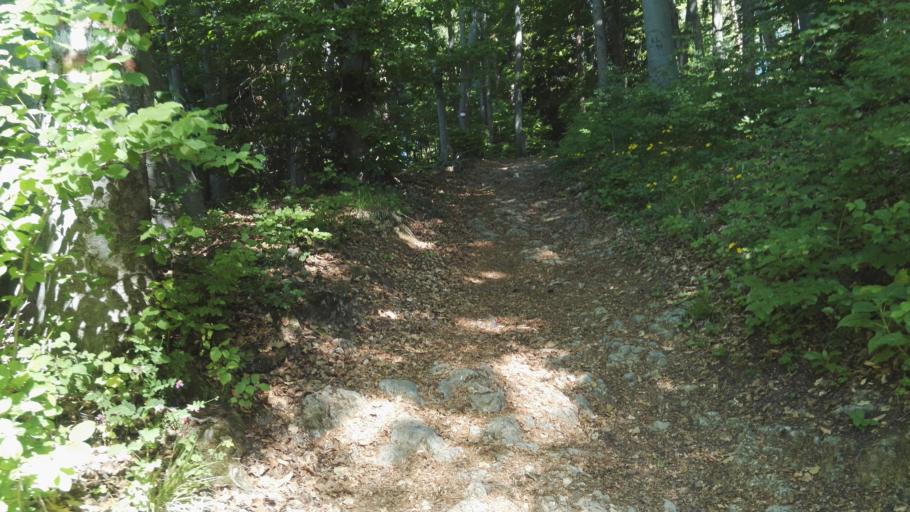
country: AT
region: Styria
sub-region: Politischer Bezirk Graz-Umgebung
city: Thal
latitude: 47.0729
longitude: 15.3701
